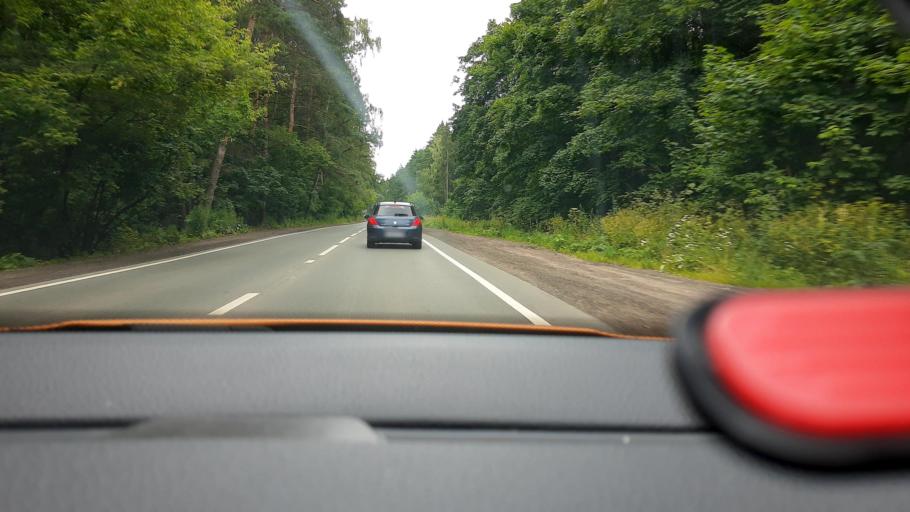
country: RU
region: Moskovskaya
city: Pirogovskiy
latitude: 55.9917
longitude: 37.7272
